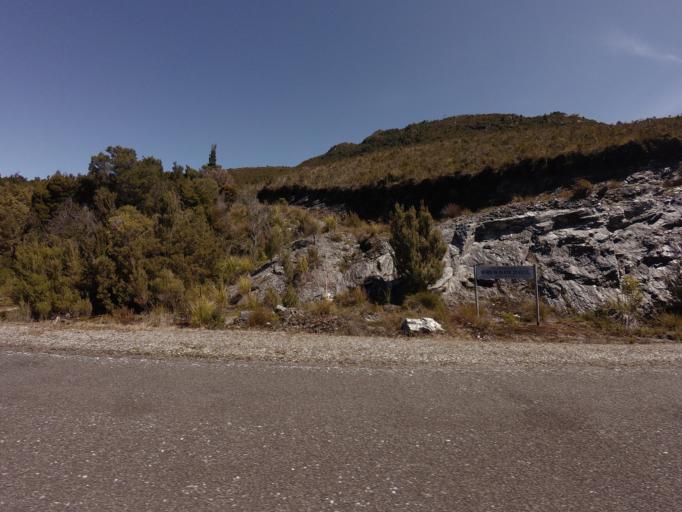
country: AU
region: Tasmania
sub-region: West Coast
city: Queenstown
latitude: -42.7523
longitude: 145.9809
